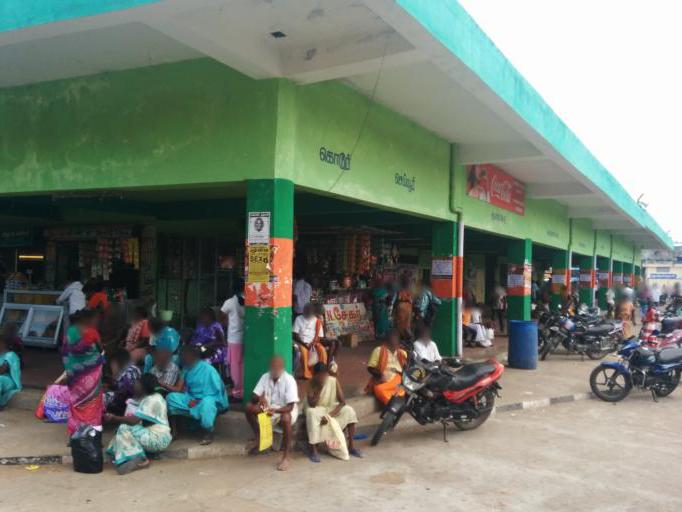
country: IN
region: Tamil Nadu
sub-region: Kancheepuram
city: Madurantakam
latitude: 12.5125
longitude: 79.8849
